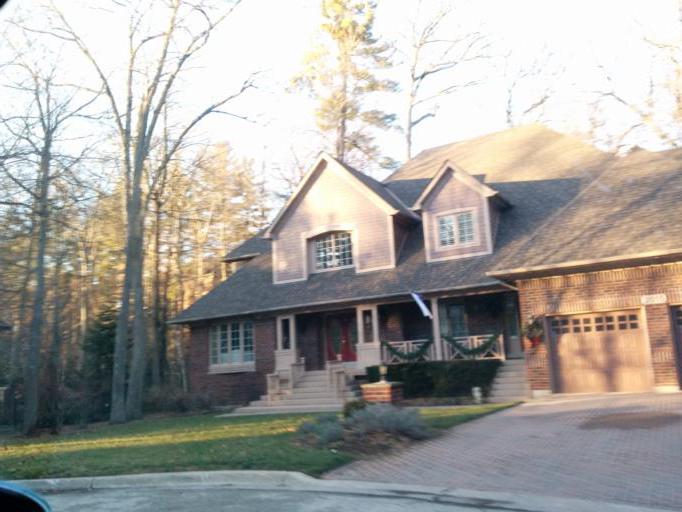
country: CA
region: Ontario
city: Mississauga
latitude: 43.5581
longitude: -79.6117
